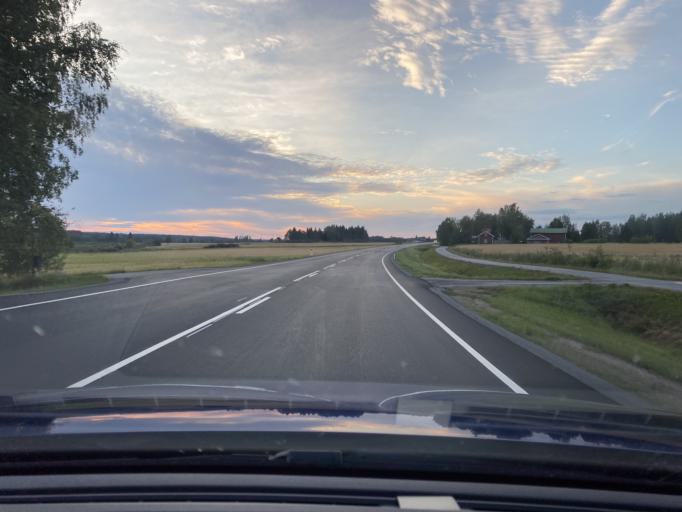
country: FI
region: Satakunta
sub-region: Pohjois-Satakunta
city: Kankaanpaeae
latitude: 61.8451
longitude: 22.3360
